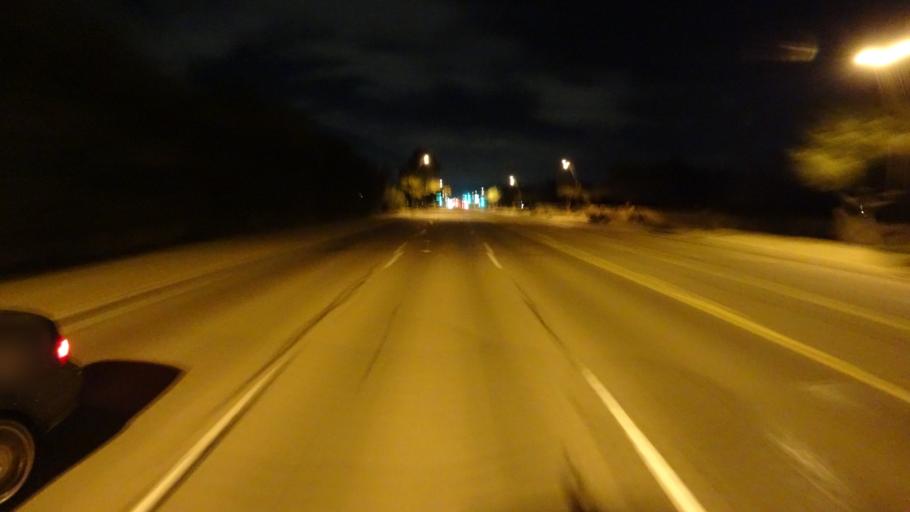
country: US
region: Arizona
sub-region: Maricopa County
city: Guadalupe
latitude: 33.3396
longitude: -111.9286
